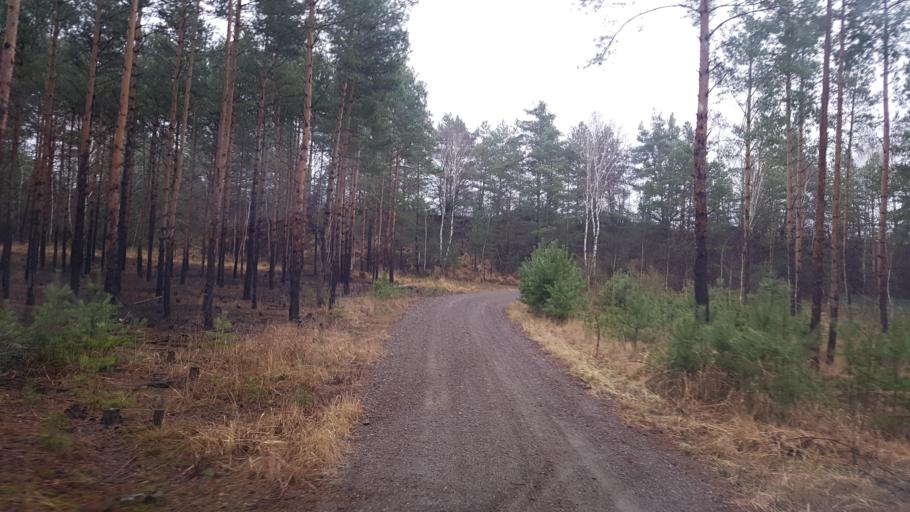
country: DE
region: Brandenburg
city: Lauchhammer
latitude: 51.5264
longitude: 13.7088
